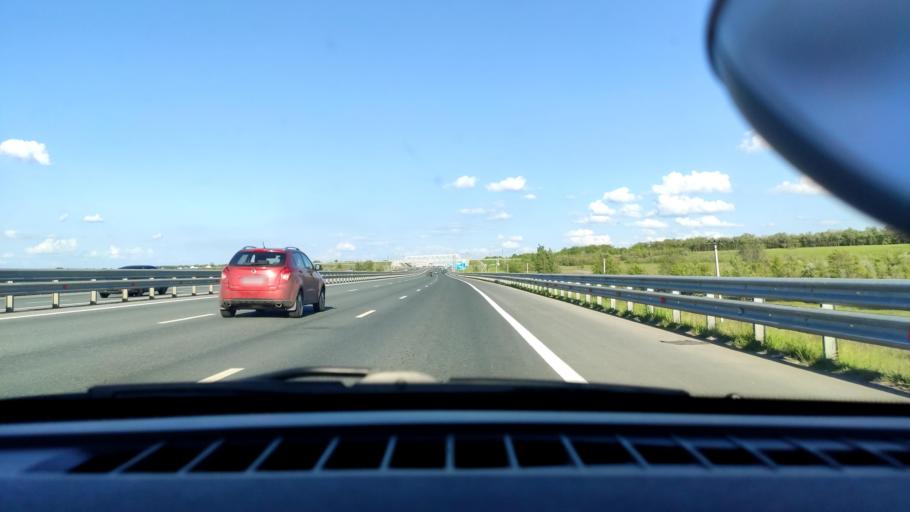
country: RU
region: Samara
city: Smyshlyayevka
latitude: 53.1498
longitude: 50.3695
